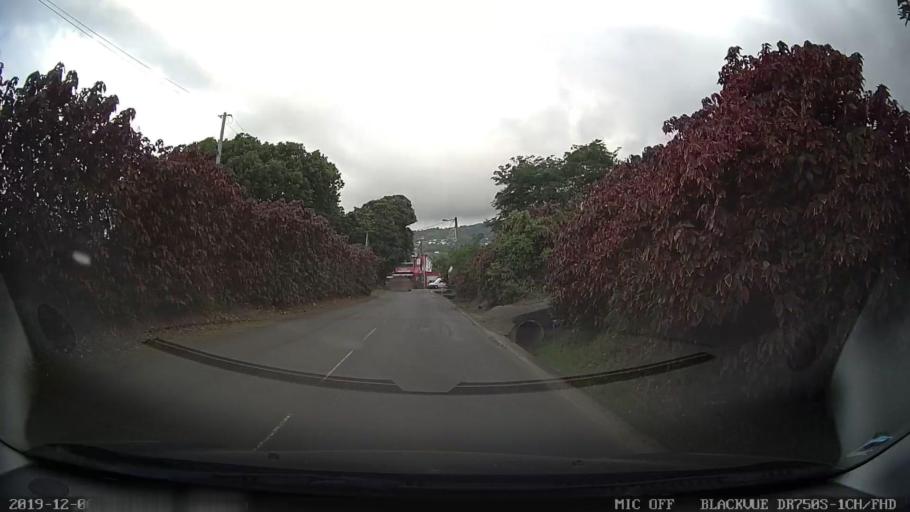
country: RE
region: Reunion
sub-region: Reunion
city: Sainte-Marie
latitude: -20.9295
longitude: 55.5307
